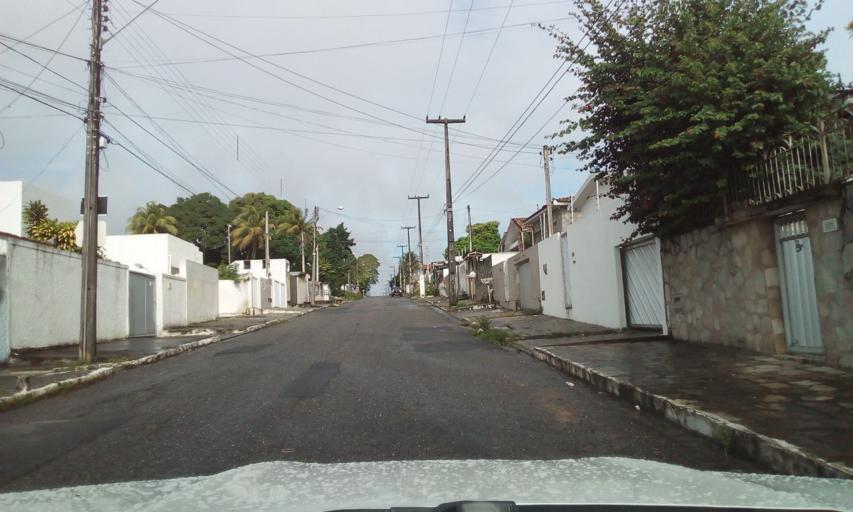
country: BR
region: Paraiba
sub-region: Joao Pessoa
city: Joao Pessoa
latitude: -7.1469
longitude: -34.8811
